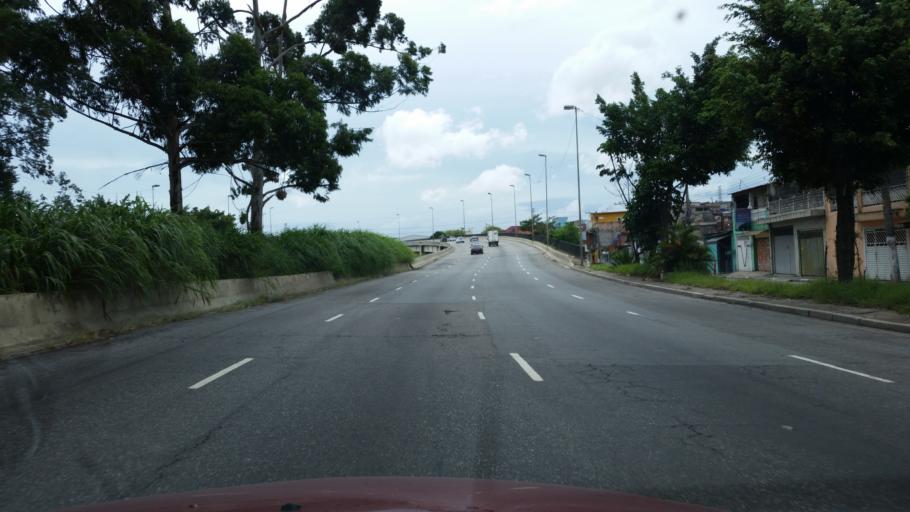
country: BR
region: Sao Paulo
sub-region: Ferraz De Vasconcelos
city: Ferraz de Vasconcelos
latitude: -23.5182
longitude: -46.4556
